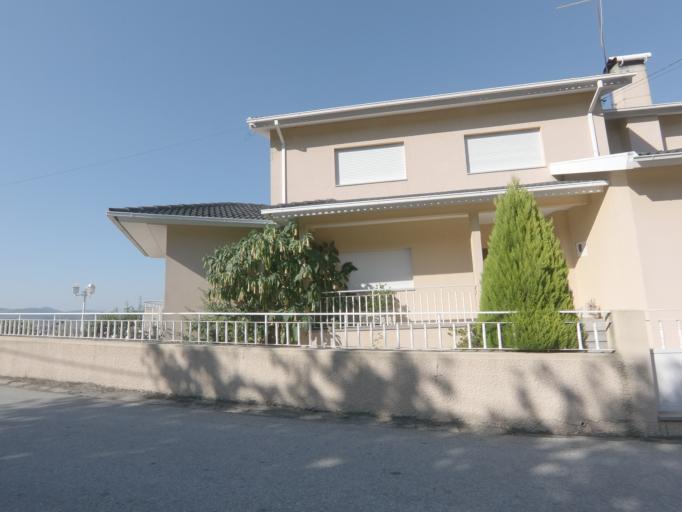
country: PT
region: Viseu
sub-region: Tabuaco
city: Tabuaco
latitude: 41.1150
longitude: -7.5623
